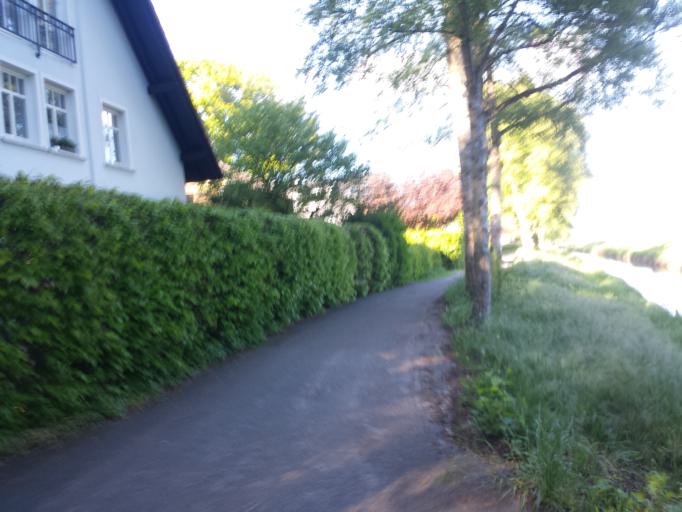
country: DE
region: Lower Saxony
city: Lilienthal
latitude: 53.1460
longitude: 8.9157
